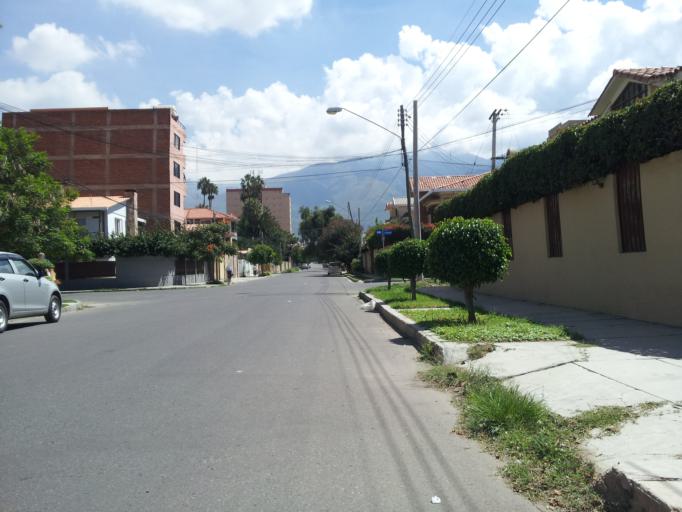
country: BO
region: Cochabamba
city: Cochabamba
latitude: -17.3786
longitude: -66.1712
